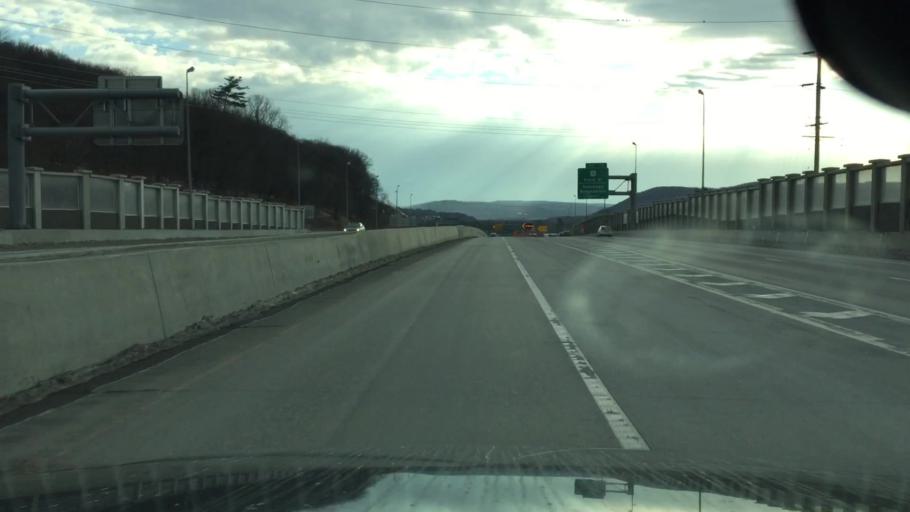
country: US
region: New York
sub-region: Broome County
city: Binghamton
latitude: 42.1127
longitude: -75.9203
